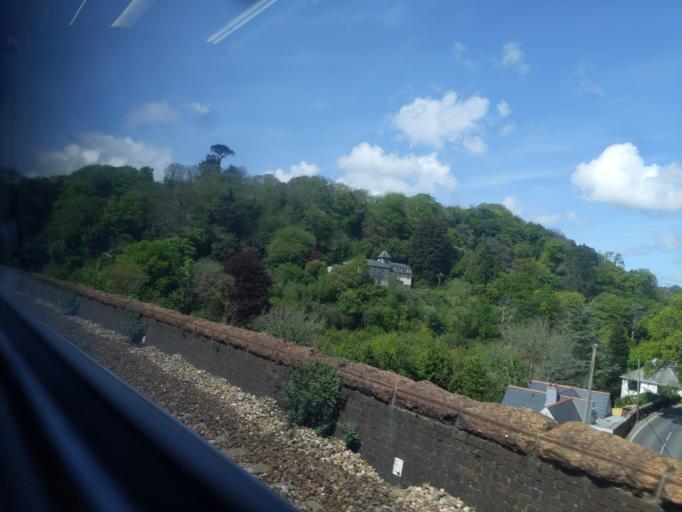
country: GB
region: England
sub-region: Cornwall
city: St Austell
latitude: 50.3422
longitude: -4.7972
